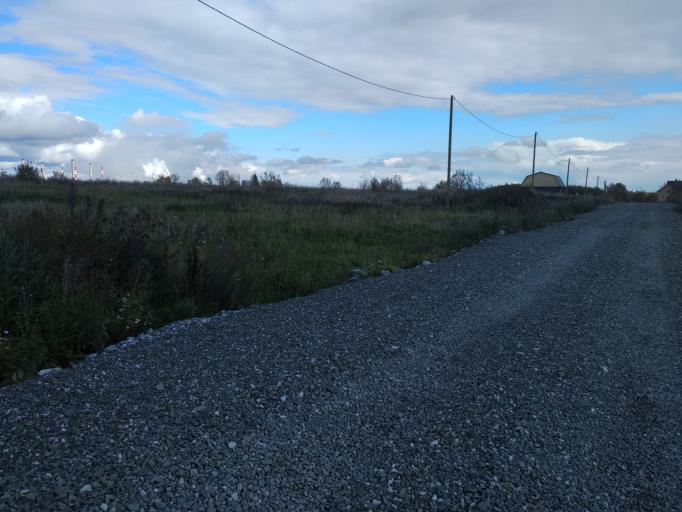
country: RU
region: Sverdlovsk
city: Krasnotur'insk
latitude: 59.7641
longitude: 60.1426
